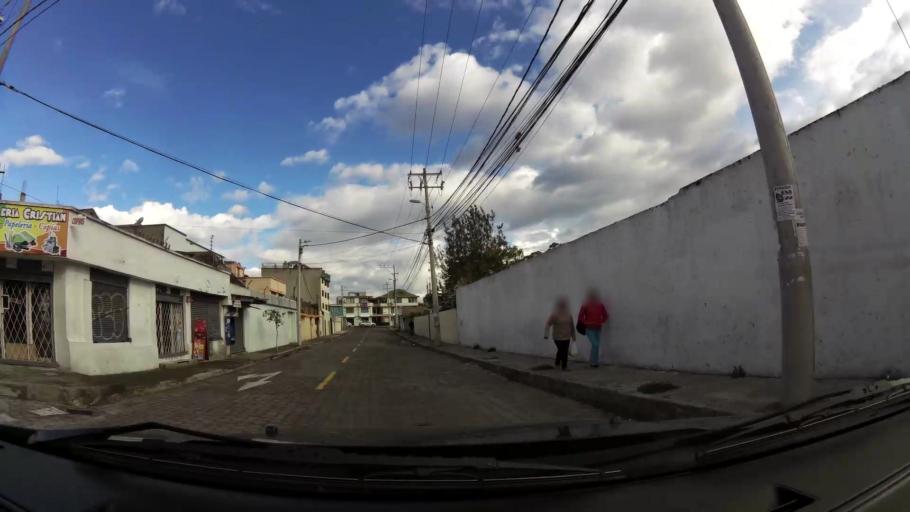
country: EC
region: Pichincha
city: Quito
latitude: -0.1335
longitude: -78.4678
